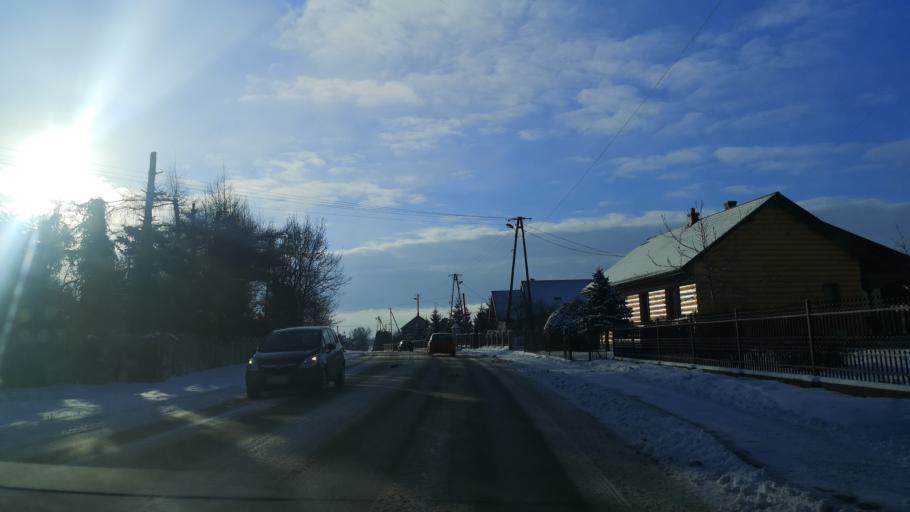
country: PL
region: Subcarpathian Voivodeship
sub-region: Powiat przeworski
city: Gorliczyna
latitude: 50.0917
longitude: 22.4913
